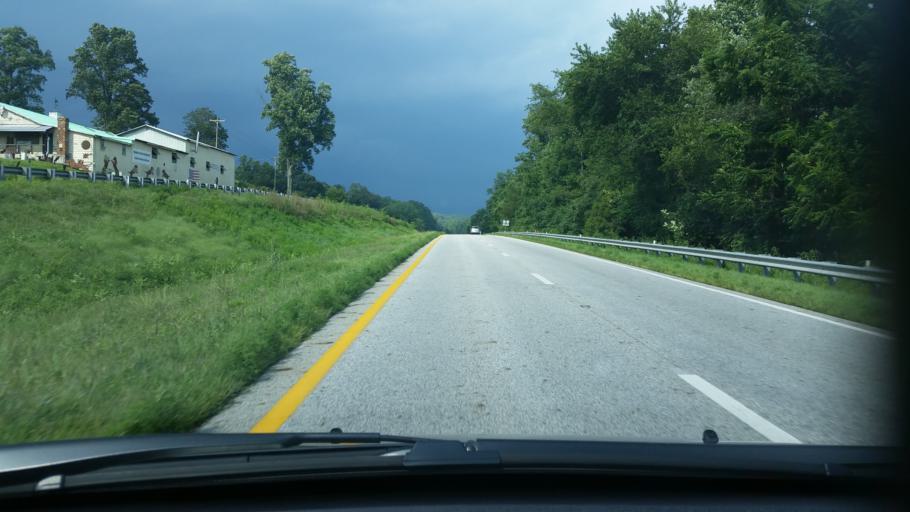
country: US
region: Virginia
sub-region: Nelson County
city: Lovingston
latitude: 37.8120
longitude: -78.8544
